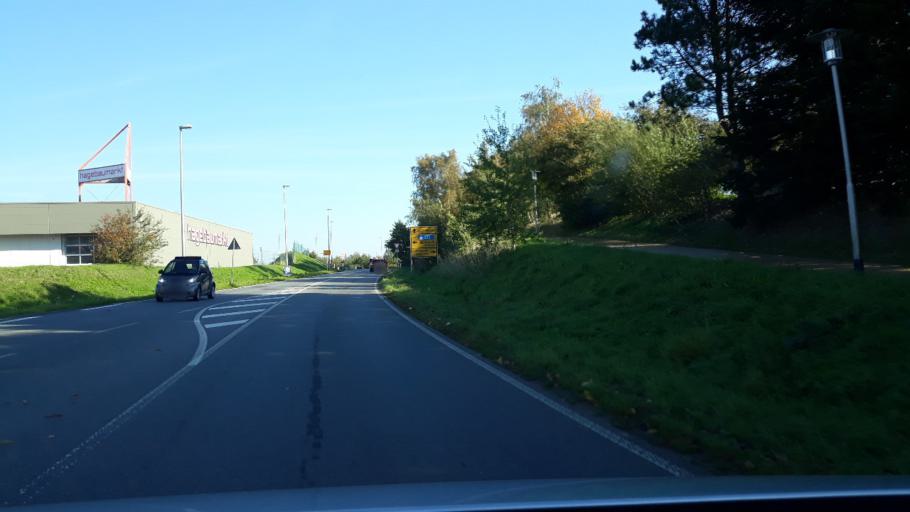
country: DE
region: Schleswig-Holstein
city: Schleswig
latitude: 54.5334
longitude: 9.5573
